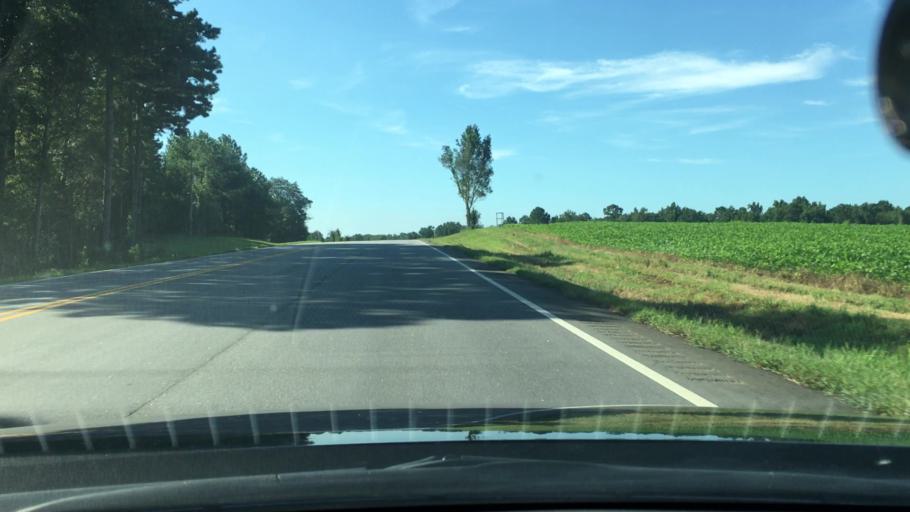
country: US
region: Georgia
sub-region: Putnam County
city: Jefferson
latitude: 33.4503
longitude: -83.4078
